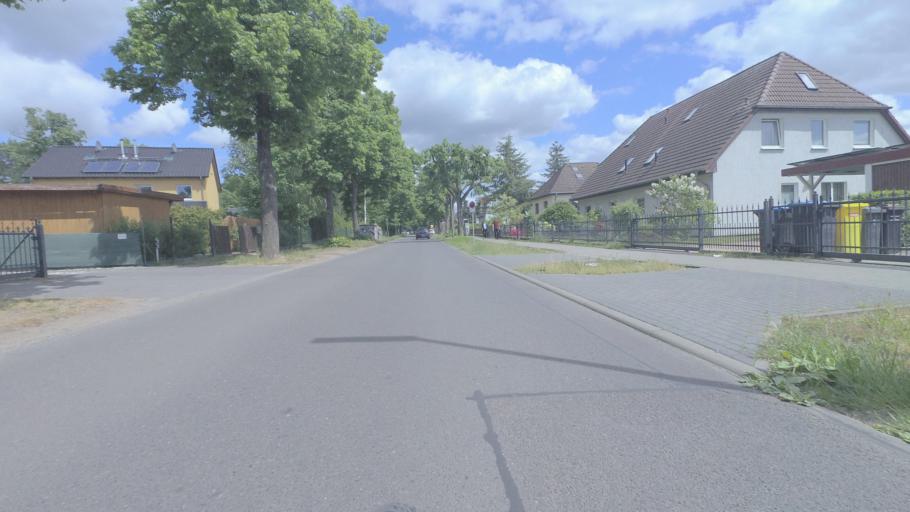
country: DE
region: Brandenburg
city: Falkensee
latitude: 52.5710
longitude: 13.1106
